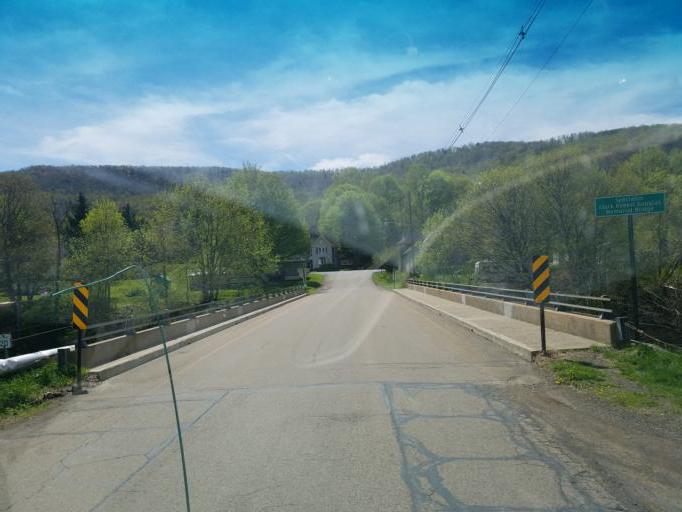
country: US
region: Pennsylvania
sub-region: Potter County
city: Galeton
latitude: 41.7373
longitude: -77.6347
